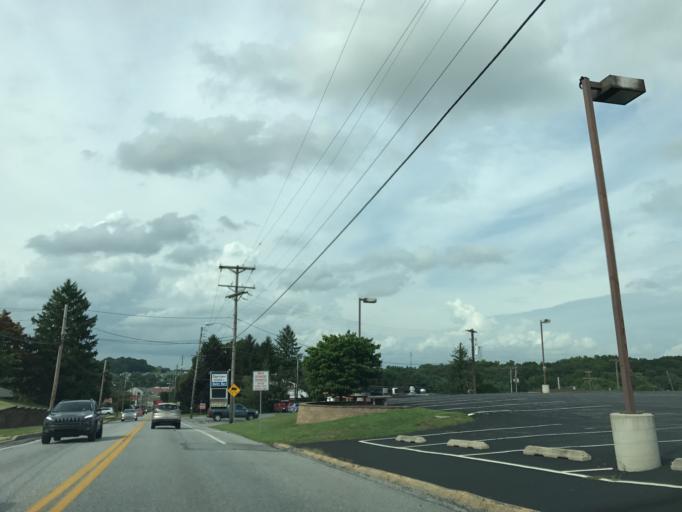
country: US
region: Pennsylvania
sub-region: York County
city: Spring Grove
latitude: 39.8789
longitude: -76.8652
